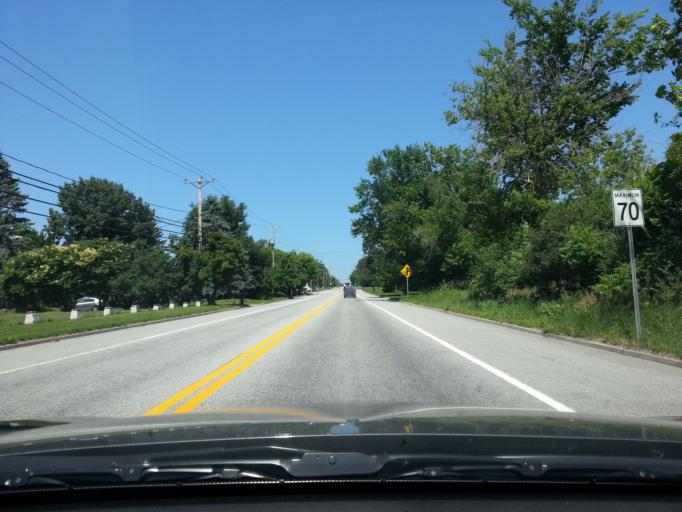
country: CA
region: Ontario
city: Bells Corners
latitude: 45.4100
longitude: -75.8697
